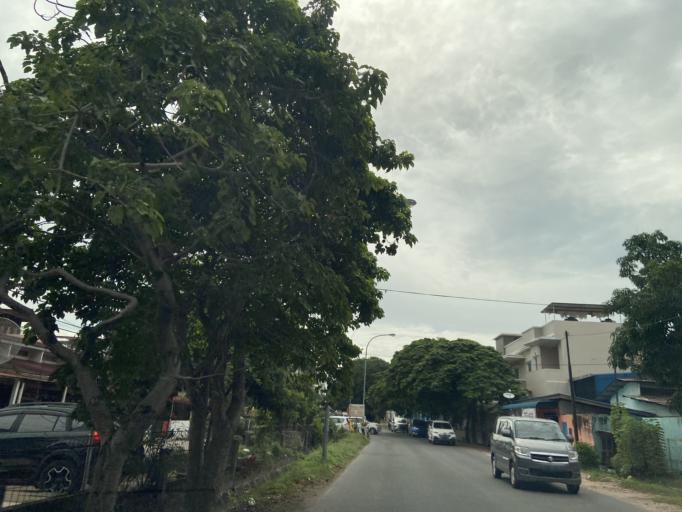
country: SG
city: Singapore
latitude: 1.1405
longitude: 104.0092
